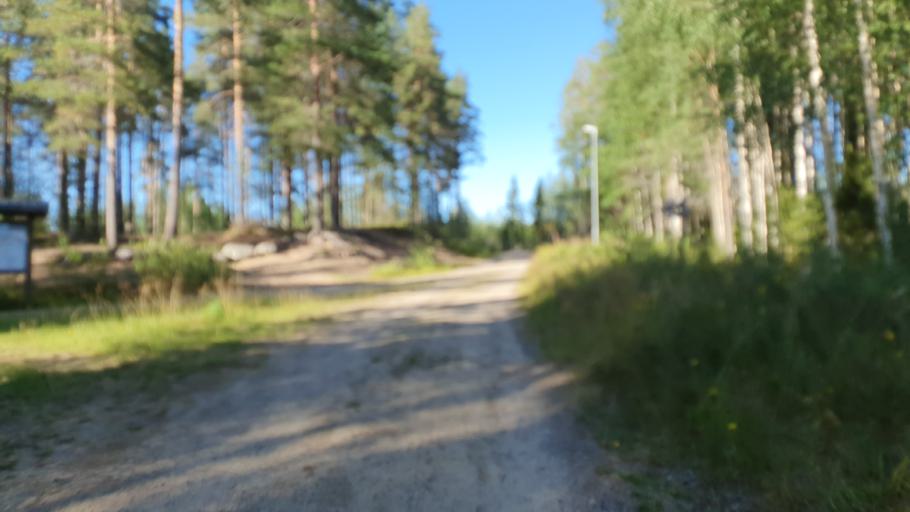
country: FI
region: Kainuu
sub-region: Kehys-Kainuu
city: Kuhmo
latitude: 64.1139
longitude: 29.5163
